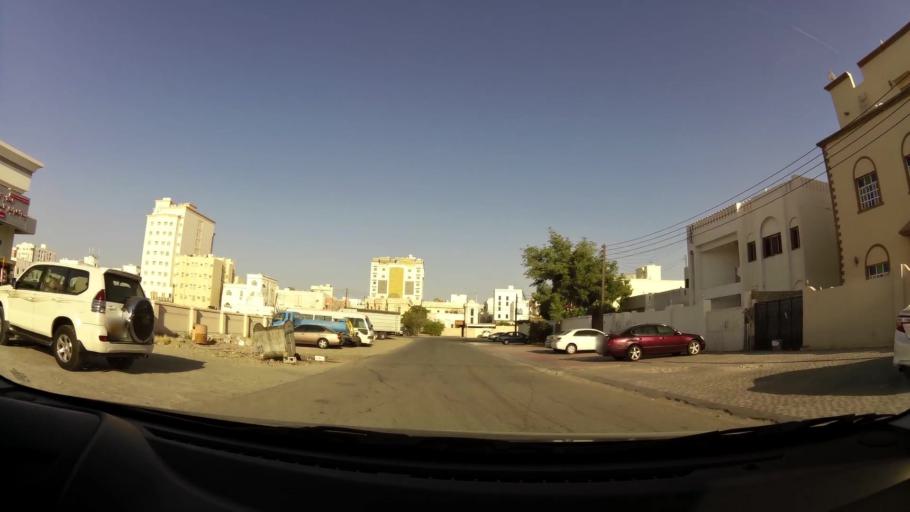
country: OM
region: Muhafazat Masqat
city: As Sib al Jadidah
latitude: 23.6310
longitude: 58.1960
